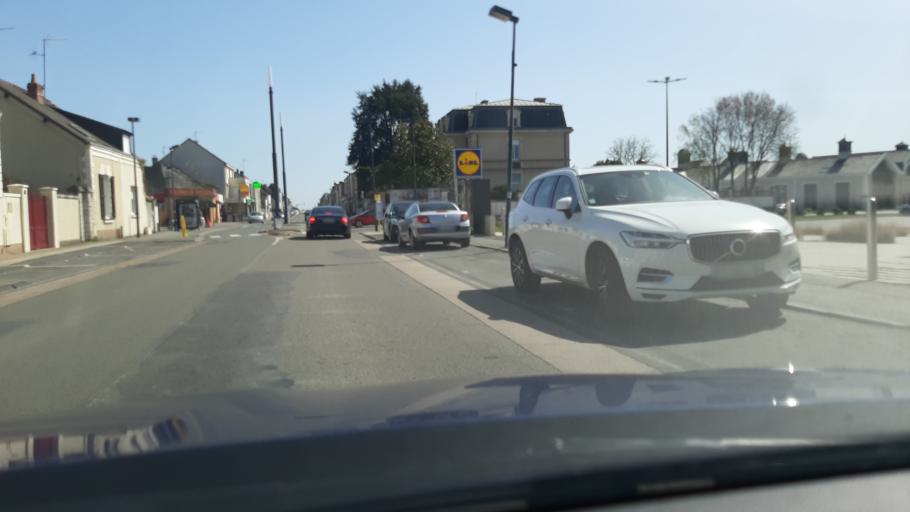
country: FR
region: Pays de la Loire
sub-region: Departement de Maine-et-Loire
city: Les Ponts-de-Ce
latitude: 47.4453
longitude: -0.5030
